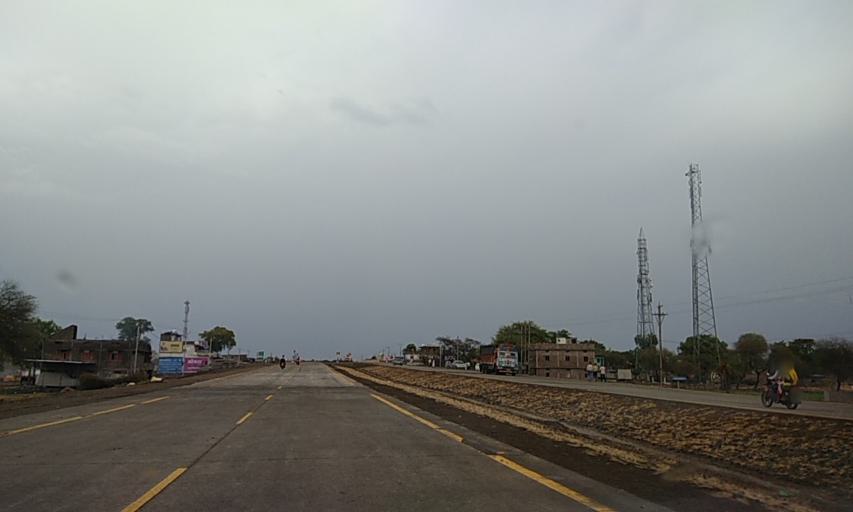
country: IN
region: Madhya Pradesh
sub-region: Rajgarh
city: Sarangpur
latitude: 23.6244
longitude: 76.5634
